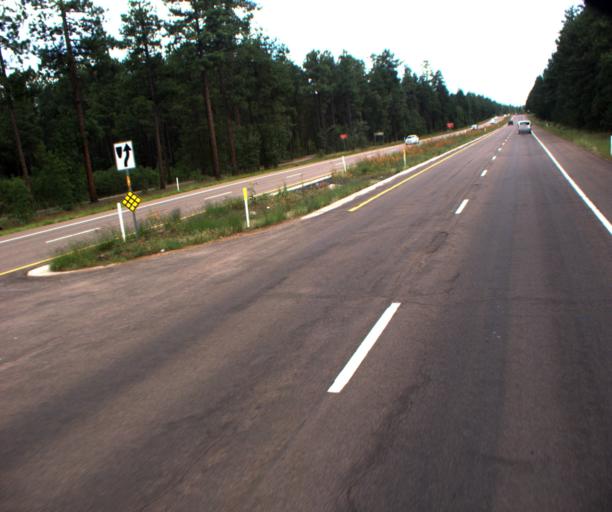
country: US
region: Arizona
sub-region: Navajo County
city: Pinetop-Lakeside
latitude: 34.1115
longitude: -109.9138
